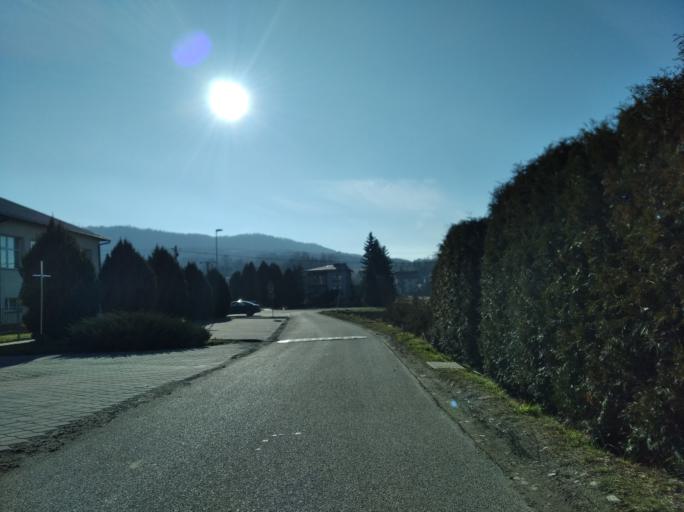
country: PL
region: Subcarpathian Voivodeship
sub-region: Powiat strzyzowski
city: Jawornik
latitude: 49.8057
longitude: 21.8897
